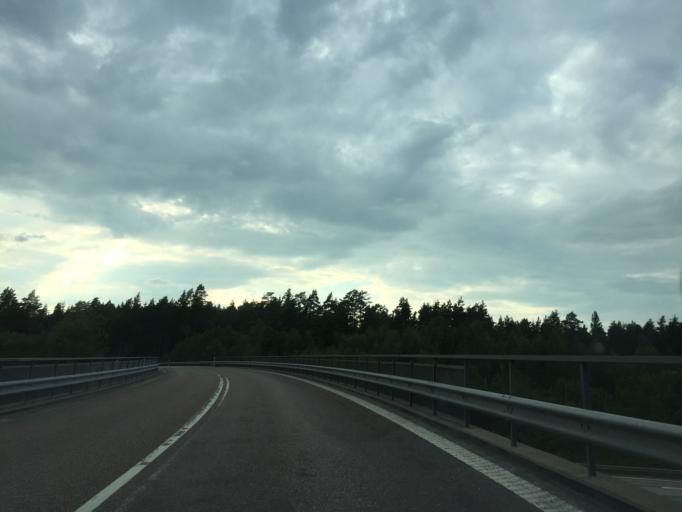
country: SE
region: OErebro
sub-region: Lindesbergs Kommun
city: Fellingsbro
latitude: 59.3401
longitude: 15.5425
